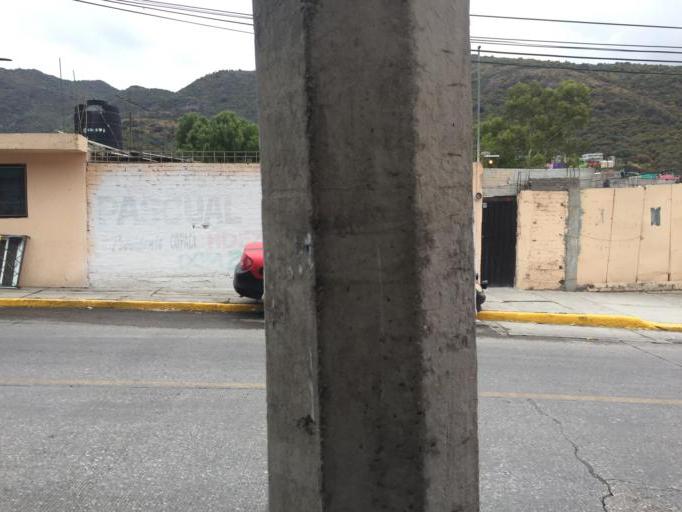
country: MX
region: Mexico
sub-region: Tlalnepantla de Baz
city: Puerto Escondido (Tepeolulco Puerto Escondido)
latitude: 19.5668
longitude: -99.0889
